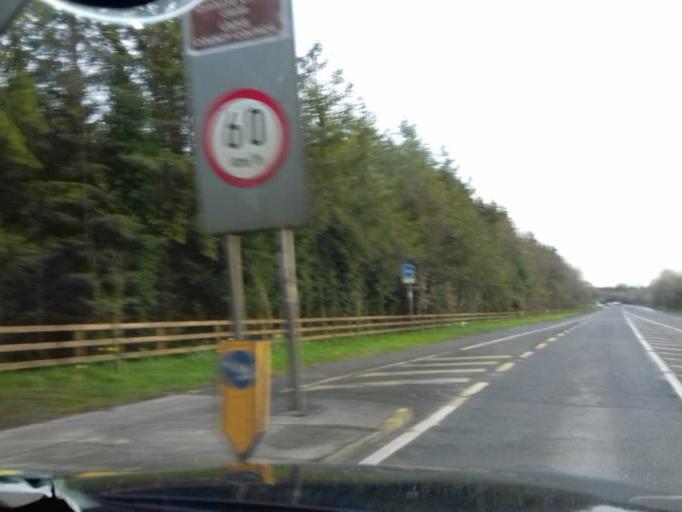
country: IE
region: Leinster
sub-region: Laois
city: Abbeyleix
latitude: 52.9040
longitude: -7.3549
